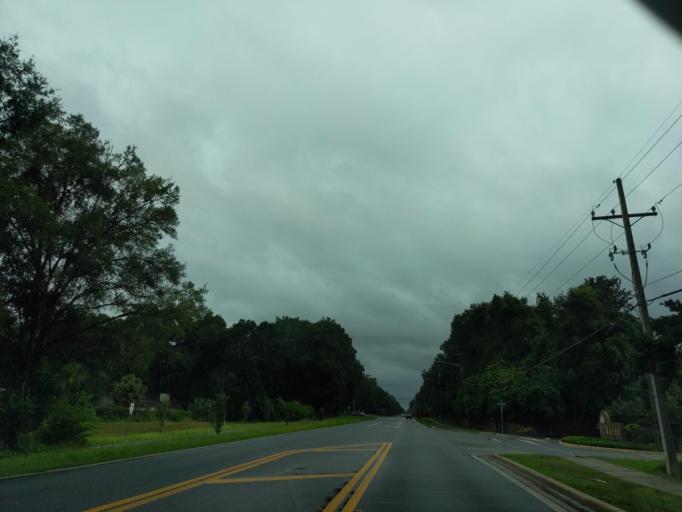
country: US
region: Florida
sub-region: Alachua County
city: Gainesville
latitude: 29.6366
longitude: -82.4225
